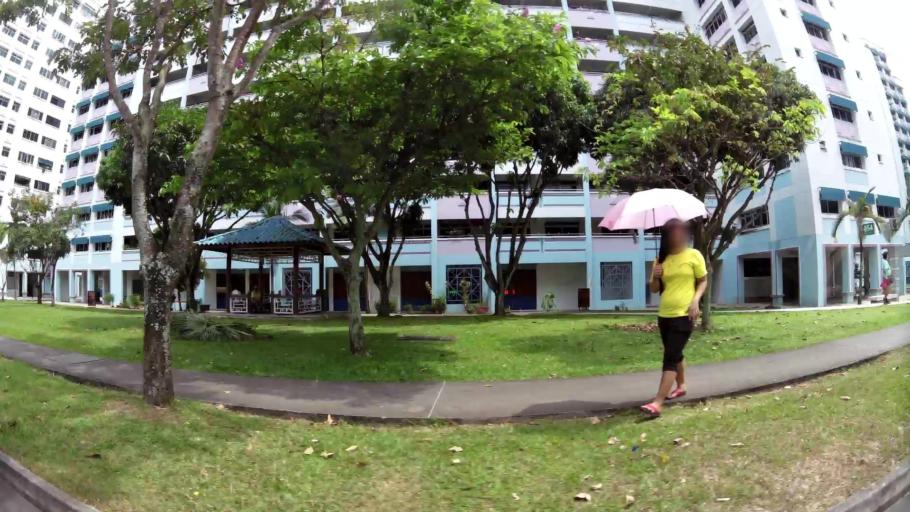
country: MY
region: Johor
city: Johor Bahru
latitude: 1.3476
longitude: 103.6957
